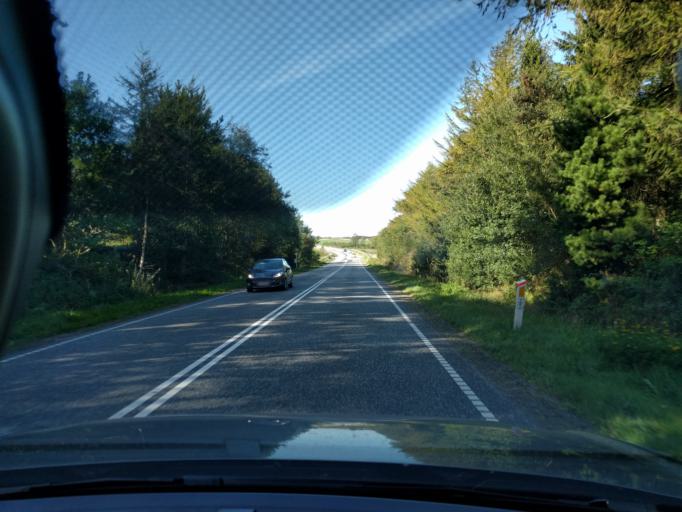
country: DK
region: North Denmark
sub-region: Mariagerfjord Kommune
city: Hobro
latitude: 56.6711
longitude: 9.7024
